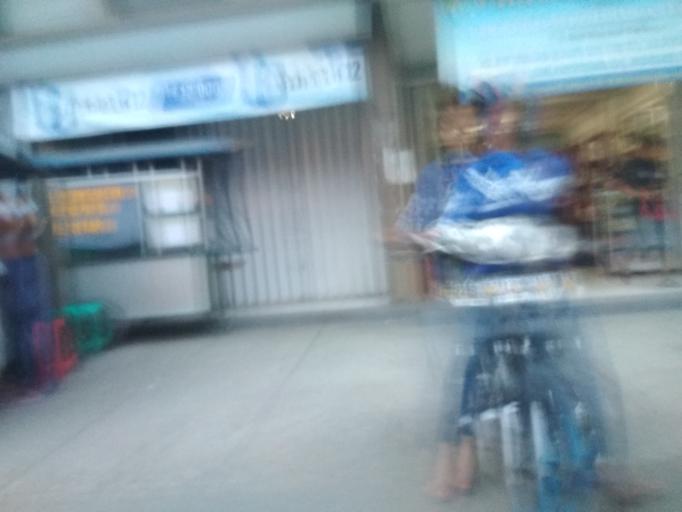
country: ID
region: West Java
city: Caringin
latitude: -6.7210
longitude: 106.8198
